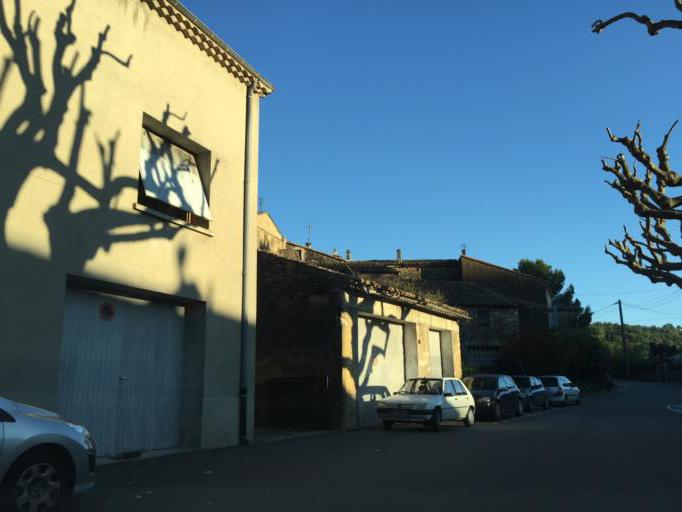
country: FR
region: Rhone-Alpes
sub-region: Departement de l'Ardeche
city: Bourg-Saint-Andeol
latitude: 44.4405
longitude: 4.6242
